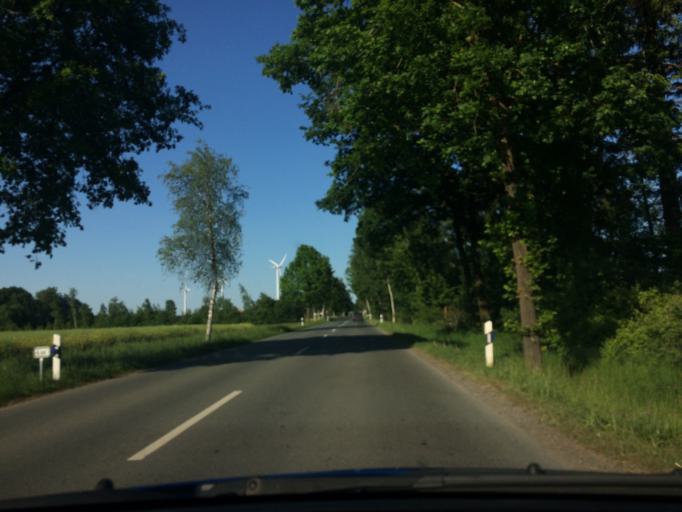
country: DE
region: Lower Saxony
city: Soltau
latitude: 53.0235
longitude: 9.9063
